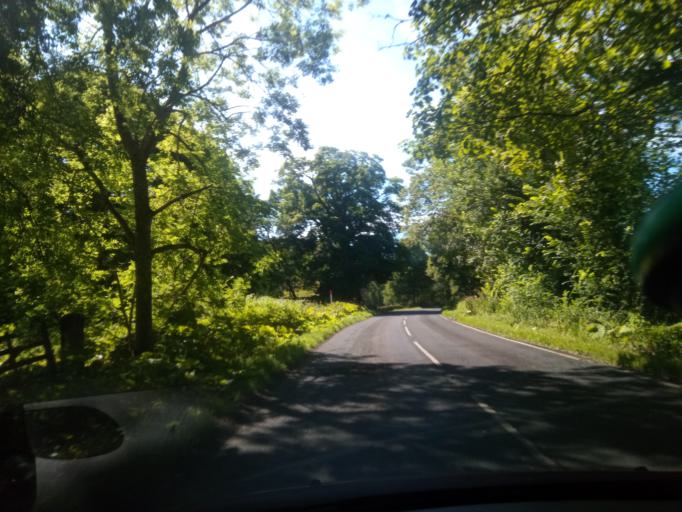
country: GB
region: England
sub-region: Northumberland
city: Bardon Mill
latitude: 54.9240
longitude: -2.3153
